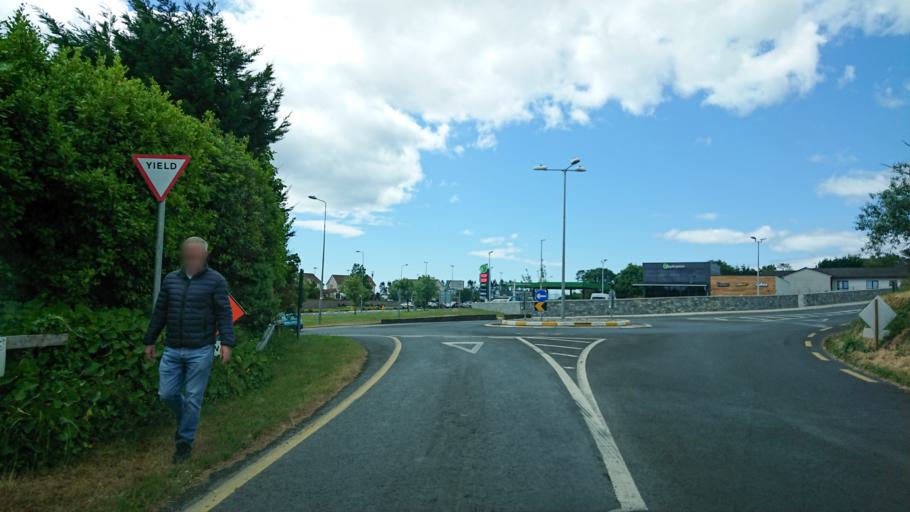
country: IE
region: Munster
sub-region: Waterford
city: Tra Mhor
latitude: 52.1732
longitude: -7.1403
